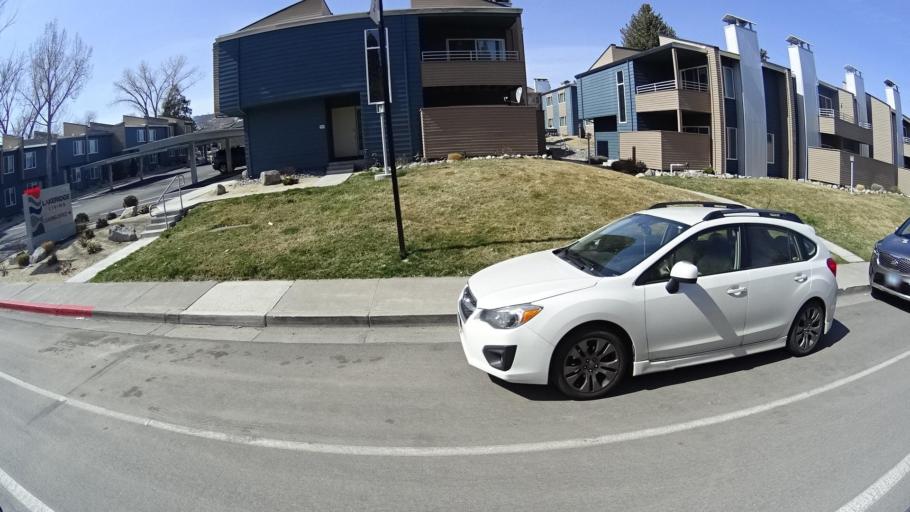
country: US
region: Nevada
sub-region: Washoe County
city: Reno
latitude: 39.4744
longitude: -119.8117
